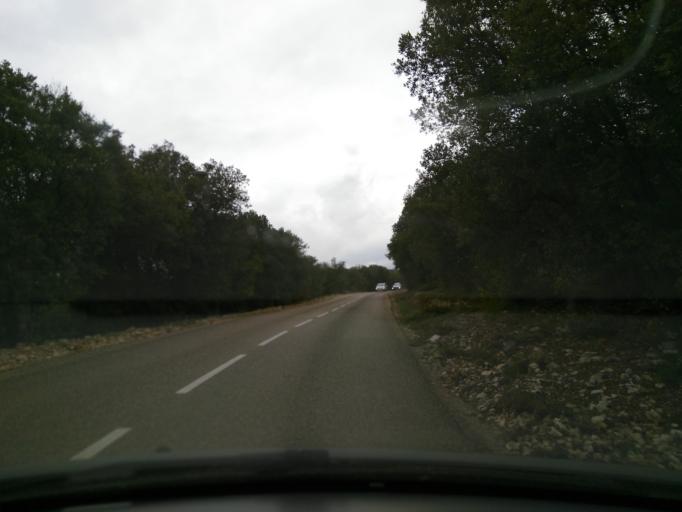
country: FR
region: Languedoc-Roussillon
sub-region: Departement du Gard
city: Barjac
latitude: 44.3216
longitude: 4.4208
